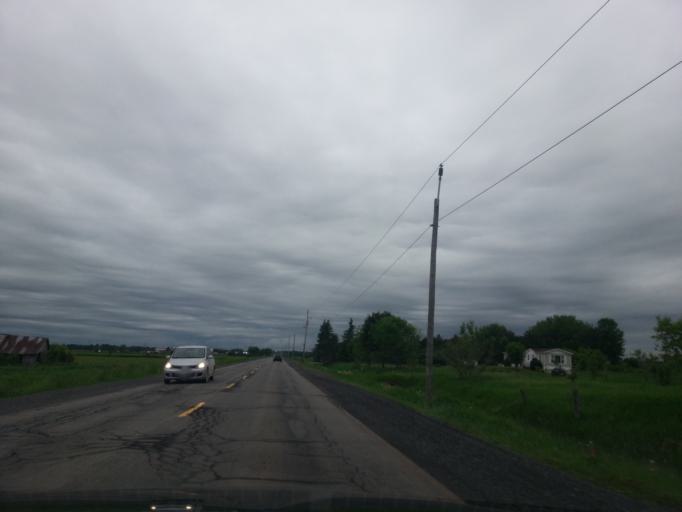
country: CA
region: Ontario
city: Bells Corners
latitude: 45.2439
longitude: -75.8625
